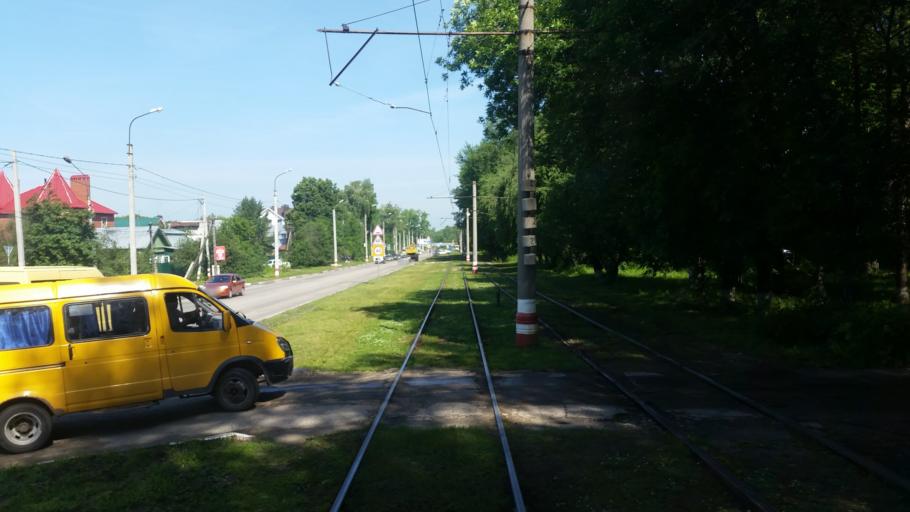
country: RU
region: Ulyanovsk
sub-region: Ulyanovskiy Rayon
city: Ulyanovsk
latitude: 54.3543
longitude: 48.3784
